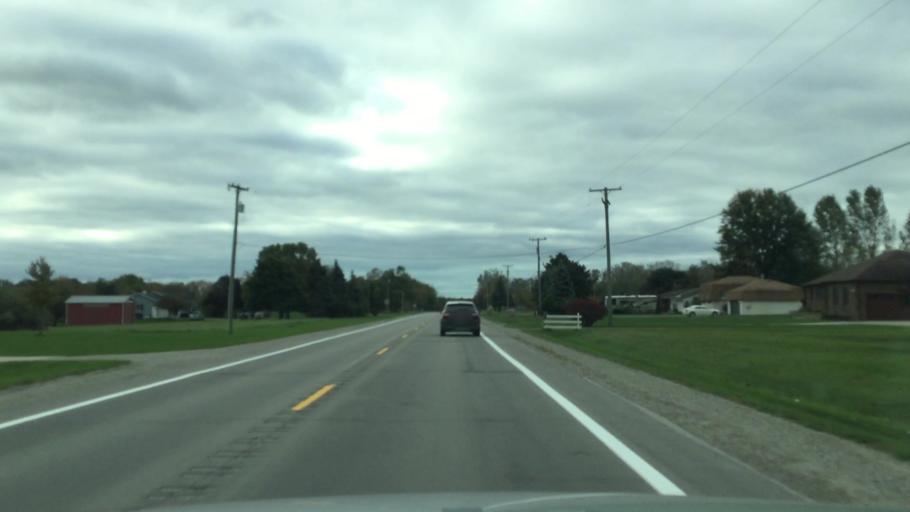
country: US
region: Michigan
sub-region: Macomb County
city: Richmond
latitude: 42.8490
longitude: -82.7629
